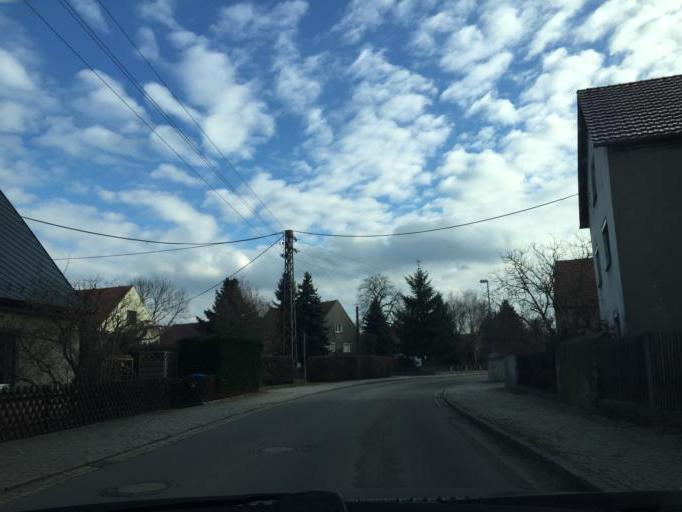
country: DE
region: Saxony
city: Ebersbach
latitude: 51.2500
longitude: 13.6600
